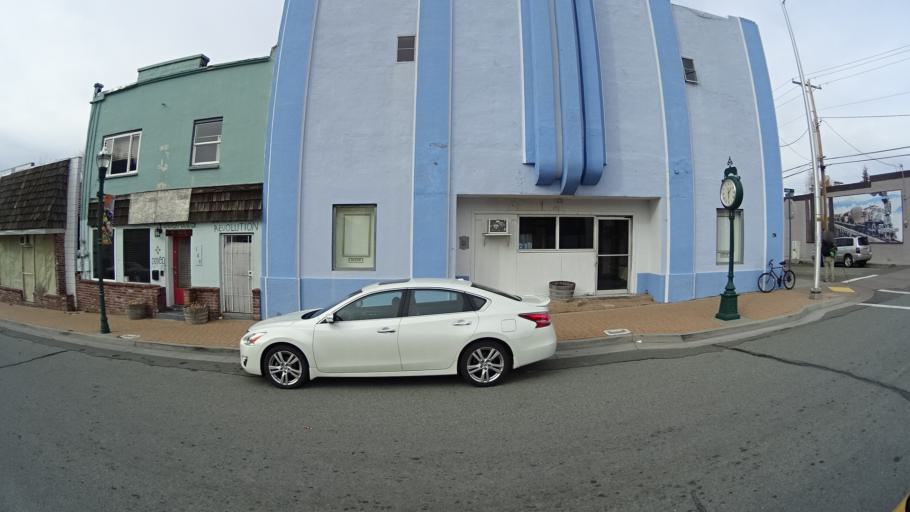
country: US
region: California
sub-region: Siskiyou County
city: Weed
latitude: 41.4238
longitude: -122.3845
